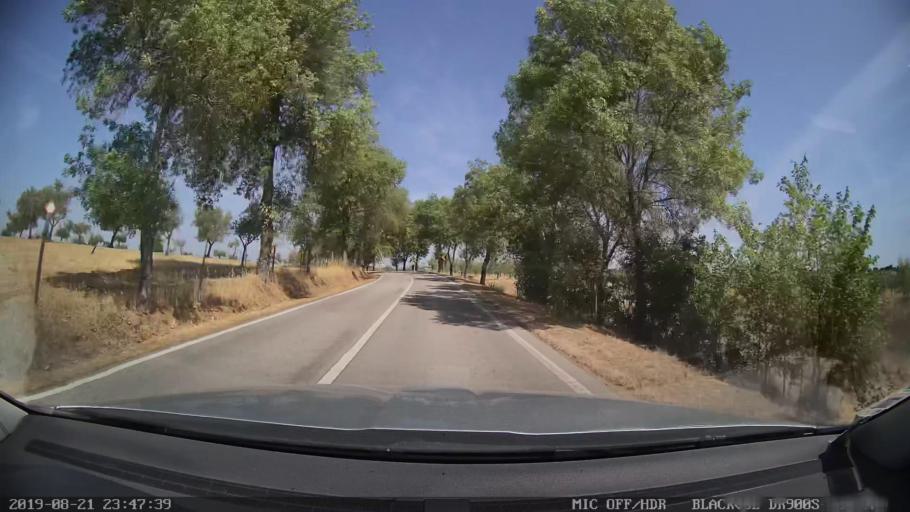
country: PT
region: Castelo Branco
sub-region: Idanha-A-Nova
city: Idanha-a-Nova
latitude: 39.8547
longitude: -7.2577
